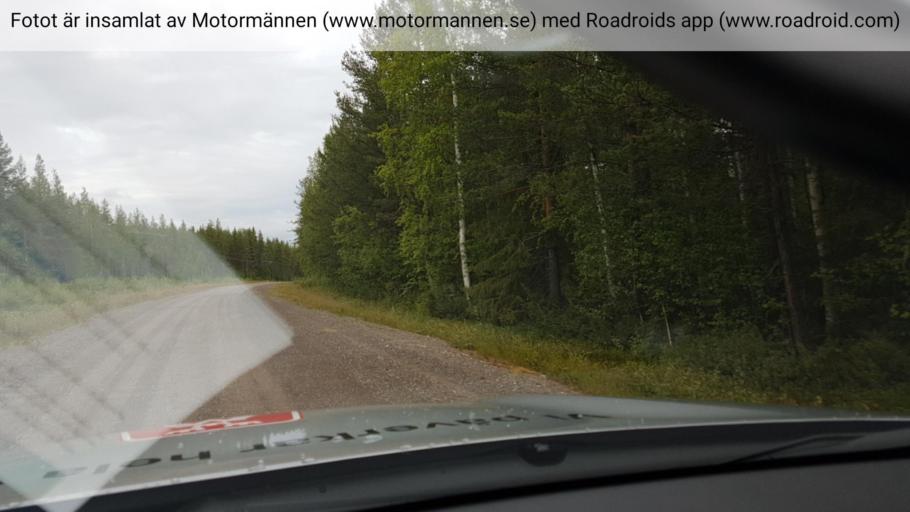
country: SE
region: Norrbotten
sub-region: Alvsbyns Kommun
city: AElvsbyn
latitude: 66.0324
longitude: 20.9945
